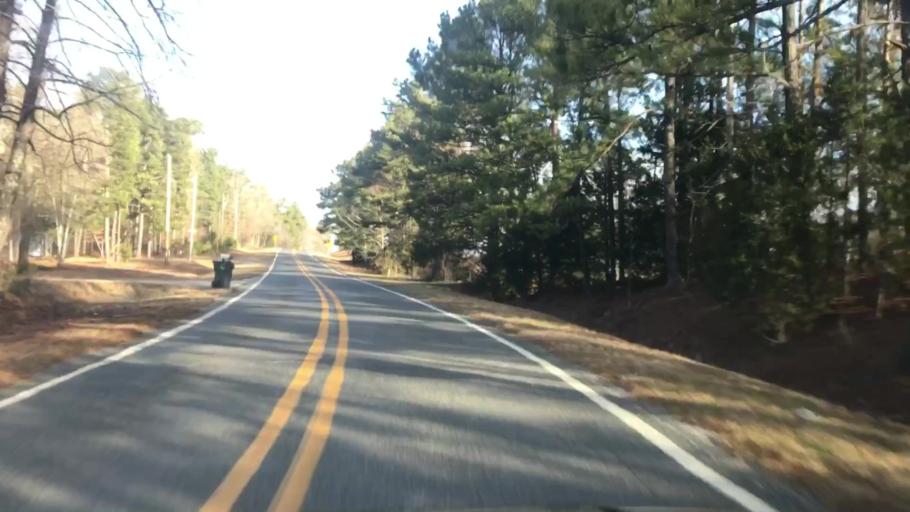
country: US
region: Arkansas
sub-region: Garland County
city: Rockwell
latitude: 34.4928
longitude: -93.2758
